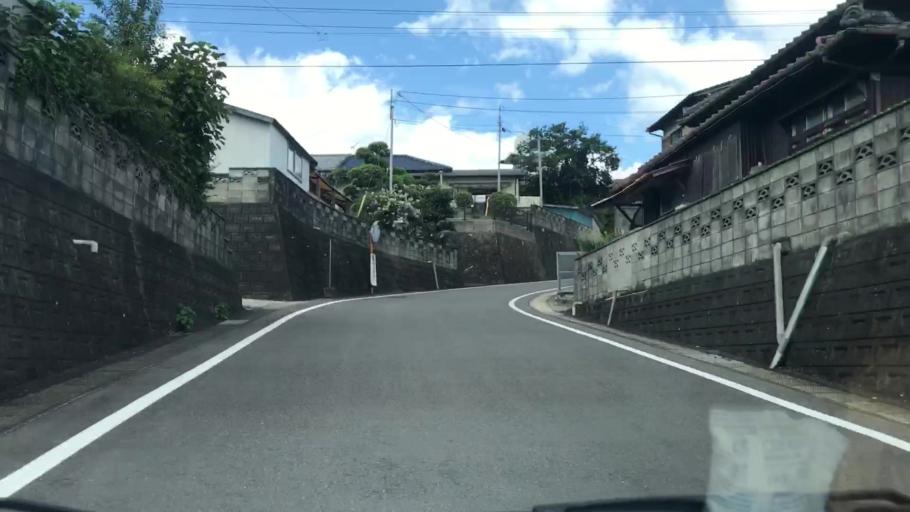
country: JP
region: Saga Prefecture
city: Takeocho-takeo
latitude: 33.2282
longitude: 130.1430
